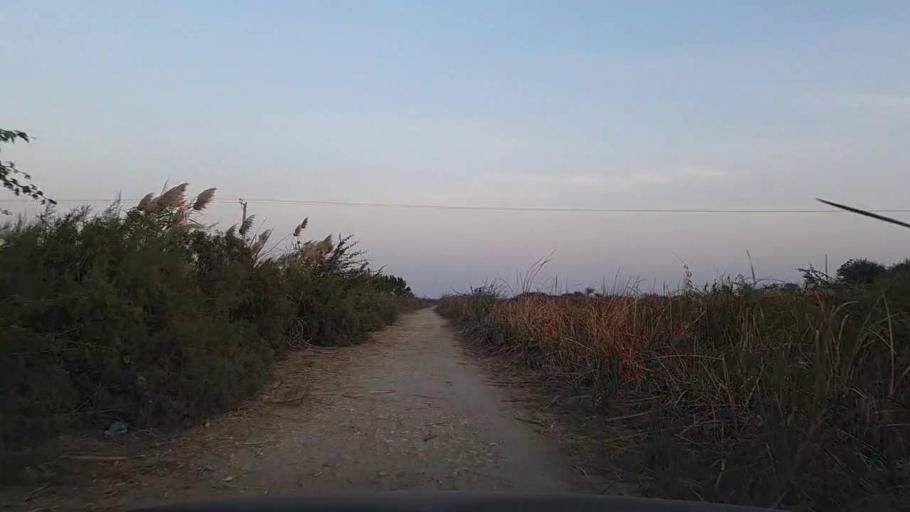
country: PK
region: Sindh
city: Tando Mittha Khan
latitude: 25.9427
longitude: 69.1348
